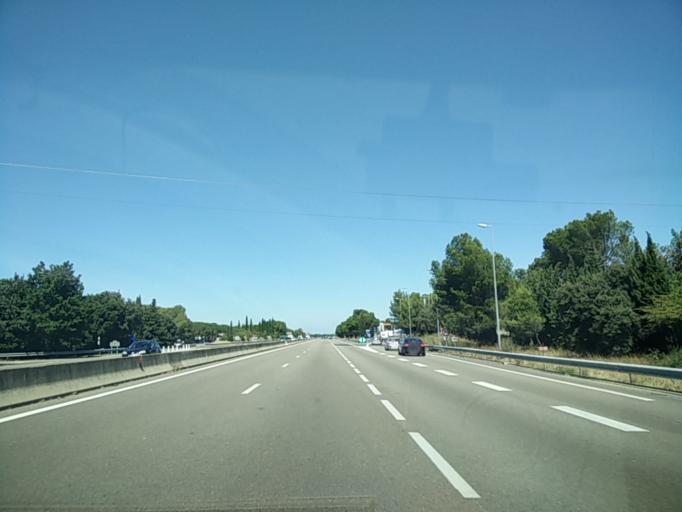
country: FR
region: Provence-Alpes-Cote d'Azur
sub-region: Departement du Vaucluse
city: Sorgues
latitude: 44.0195
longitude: 4.8894
